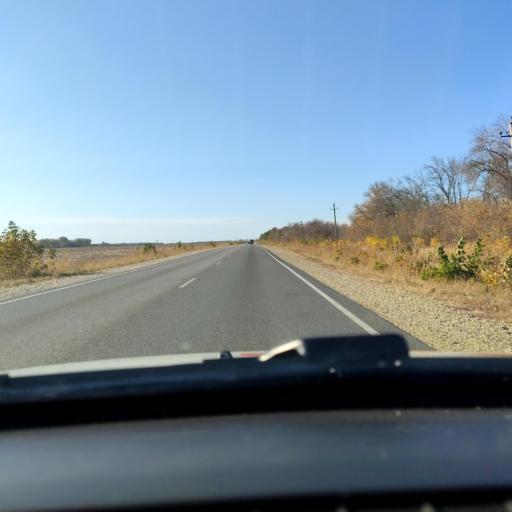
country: RU
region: Voronezj
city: Semiluki
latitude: 51.7294
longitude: 38.9798
